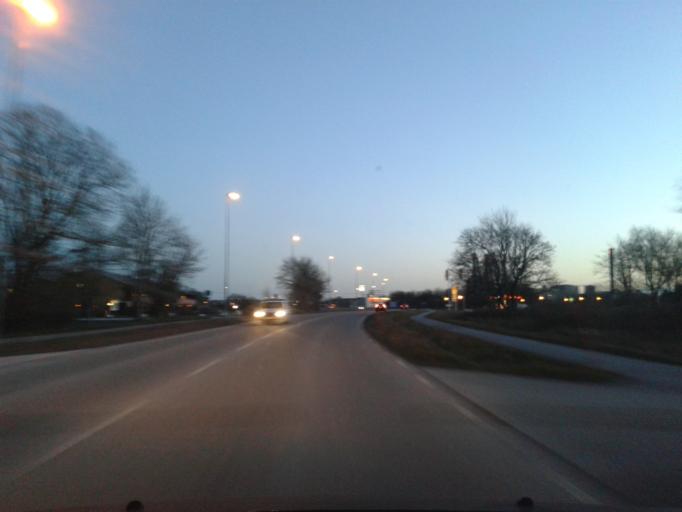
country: SE
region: Gotland
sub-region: Gotland
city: Visby
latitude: 57.6284
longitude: 18.3170
